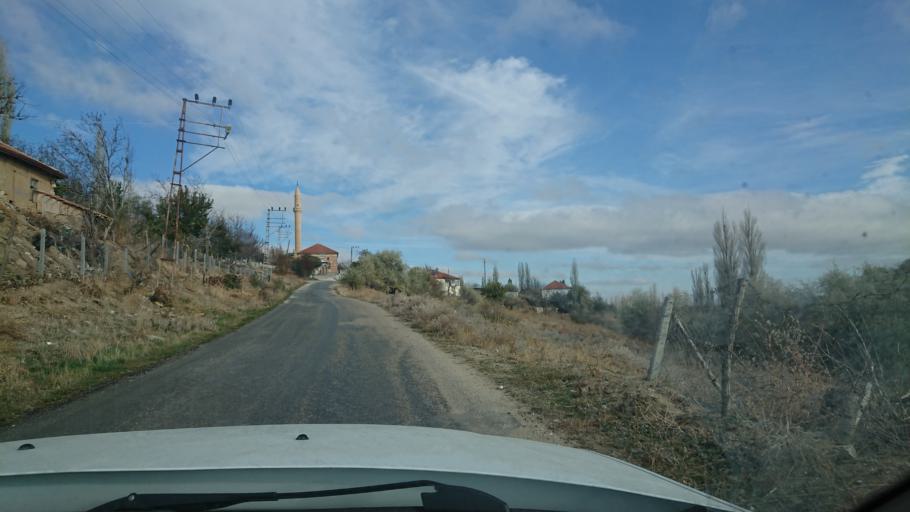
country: TR
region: Aksaray
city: Ortakoy
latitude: 38.8059
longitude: 33.9827
